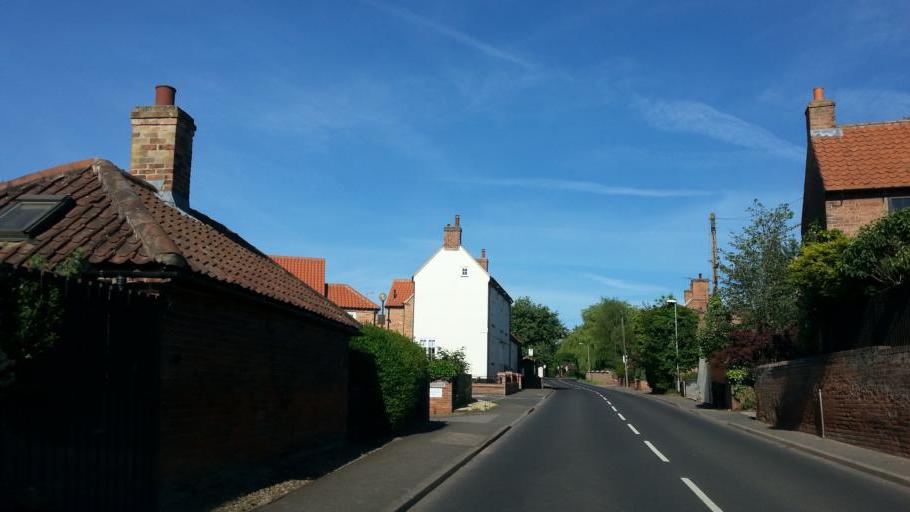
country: GB
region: England
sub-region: Nottinghamshire
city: Southwell
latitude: 53.0818
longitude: -0.8989
